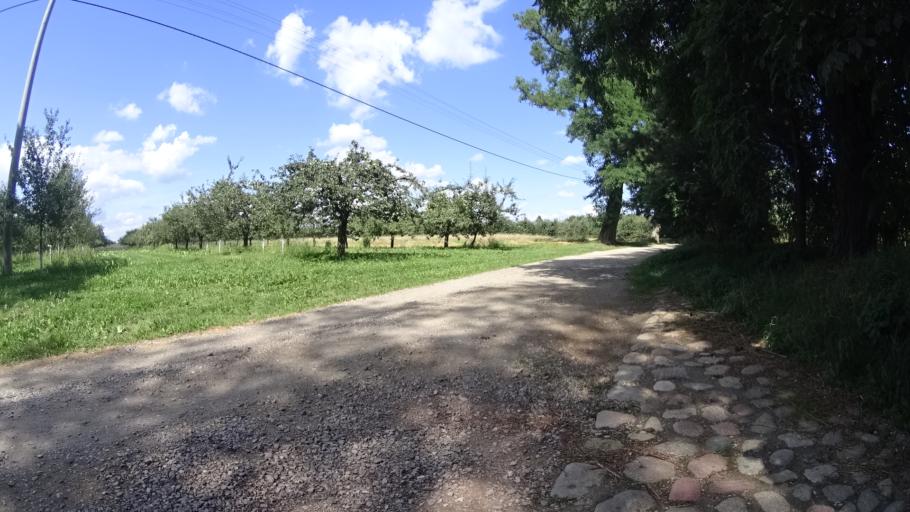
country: PL
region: Masovian Voivodeship
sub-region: Powiat grojecki
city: Mogielnica
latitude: 51.6787
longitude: 20.7586
